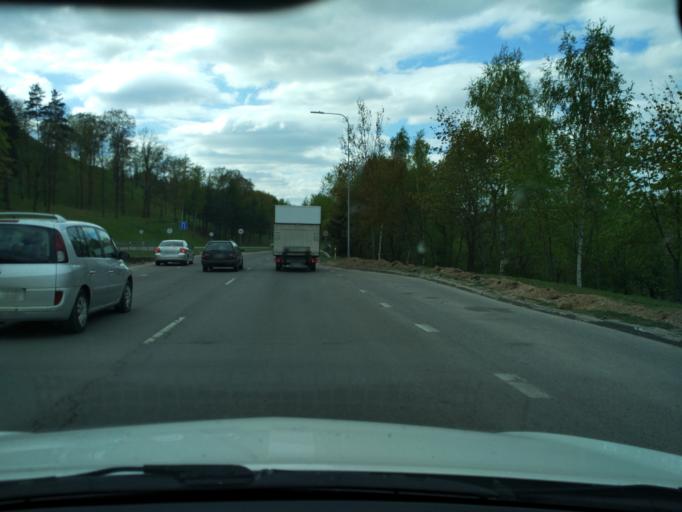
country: LT
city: Skaidiskes
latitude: 54.6903
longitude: 25.3958
